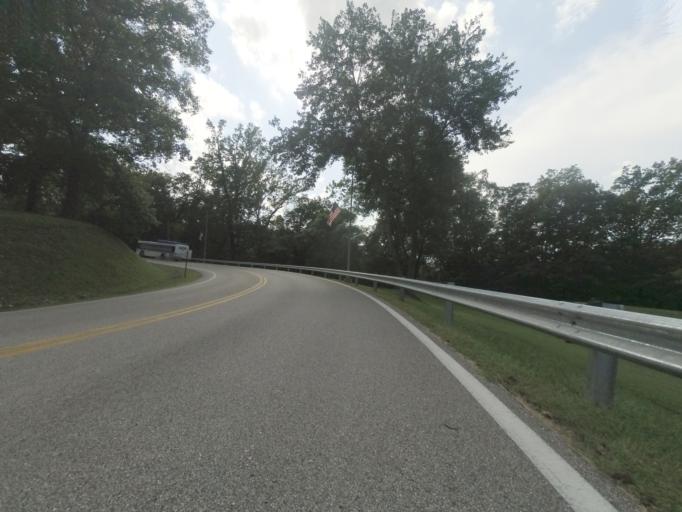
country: US
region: Ohio
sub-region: Lawrence County
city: Burlington
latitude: 38.3813
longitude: -82.5184
